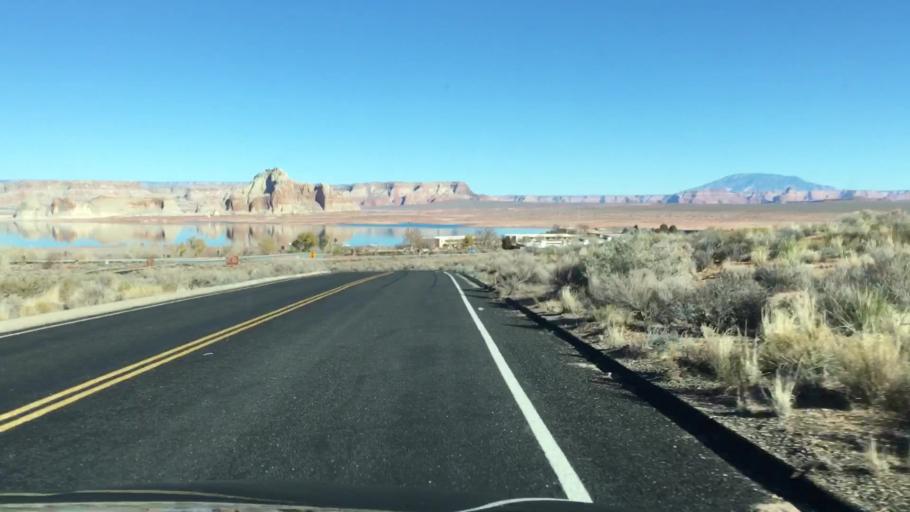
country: US
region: Arizona
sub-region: Coconino County
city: Page
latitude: 36.9935
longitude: -111.4957
